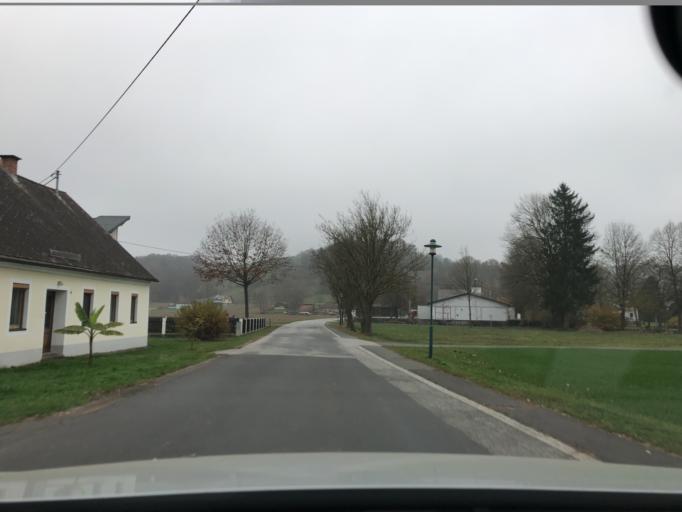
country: AT
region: Styria
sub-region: Politischer Bezirk Suedoststeiermark
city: Fehring
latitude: 46.9520
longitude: 16.0341
